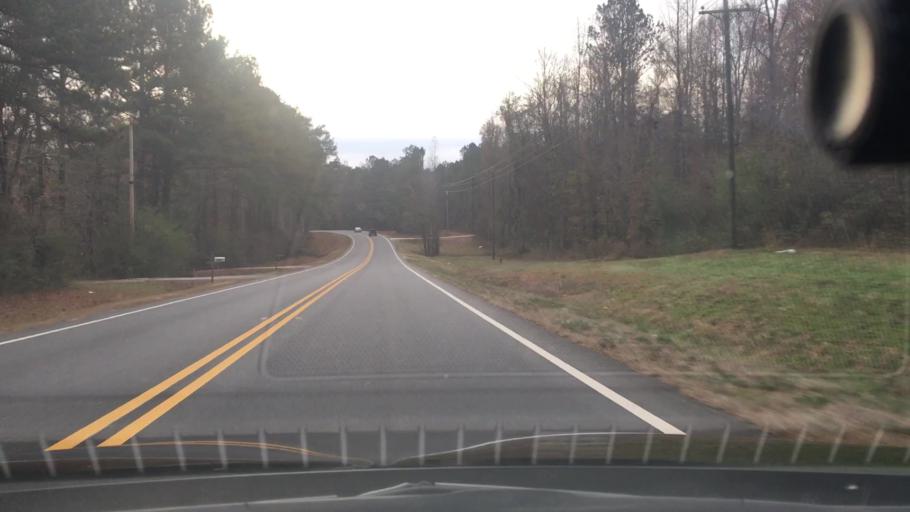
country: US
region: Georgia
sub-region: Coweta County
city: Senoia
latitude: 33.2647
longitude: -84.5198
